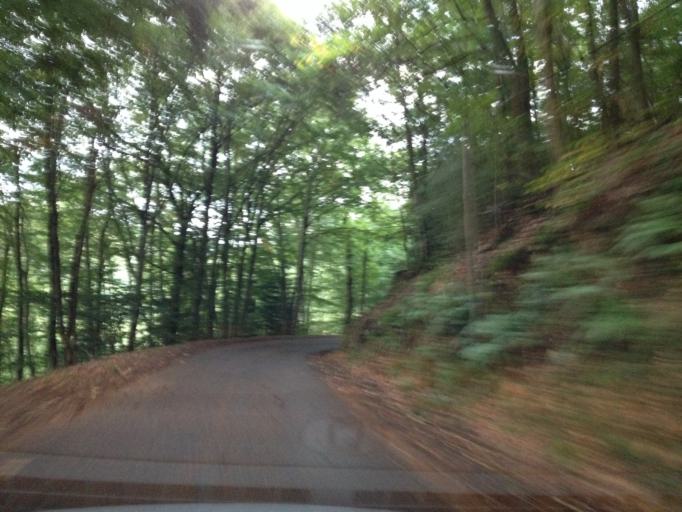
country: FR
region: Rhone-Alpes
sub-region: Departement de la Loire
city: Renaison
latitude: 46.0180
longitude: 3.8649
